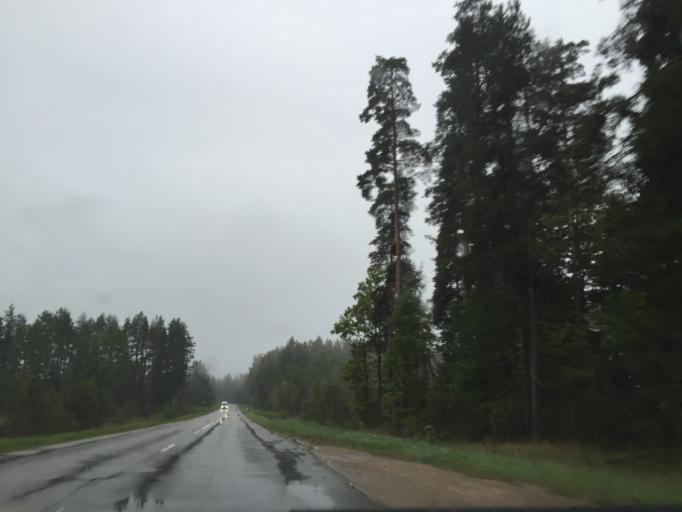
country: LV
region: Incukalns
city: Incukalns
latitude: 57.0304
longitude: 24.6827
